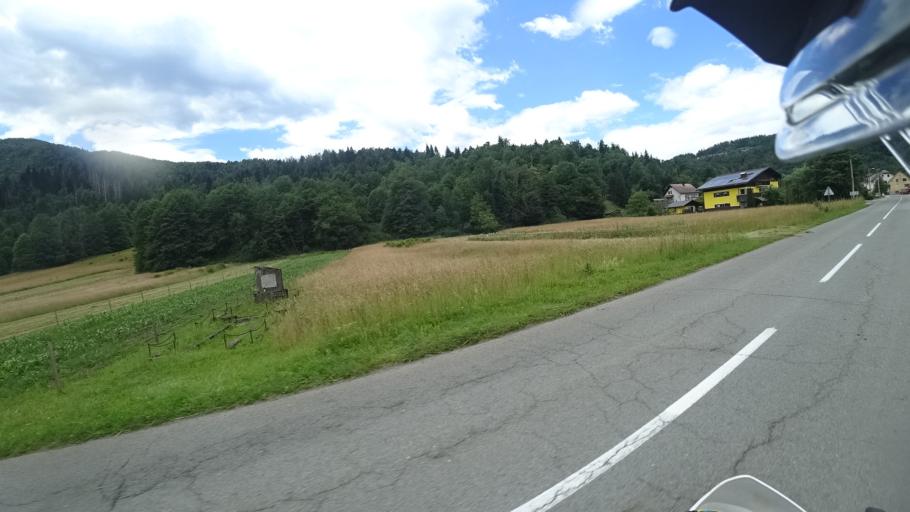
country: SI
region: Osilnica
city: Osilnica
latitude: 45.5424
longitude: 14.6872
